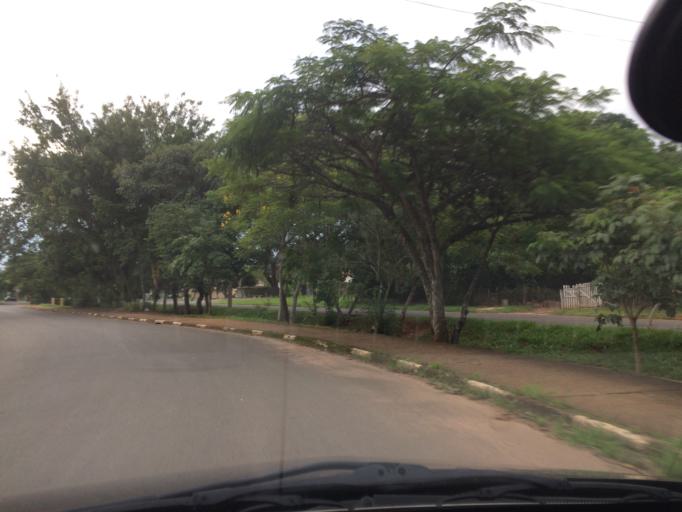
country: BR
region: Sao Paulo
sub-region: Casa Branca
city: Casa Branca
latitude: -21.7674
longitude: -47.0892
